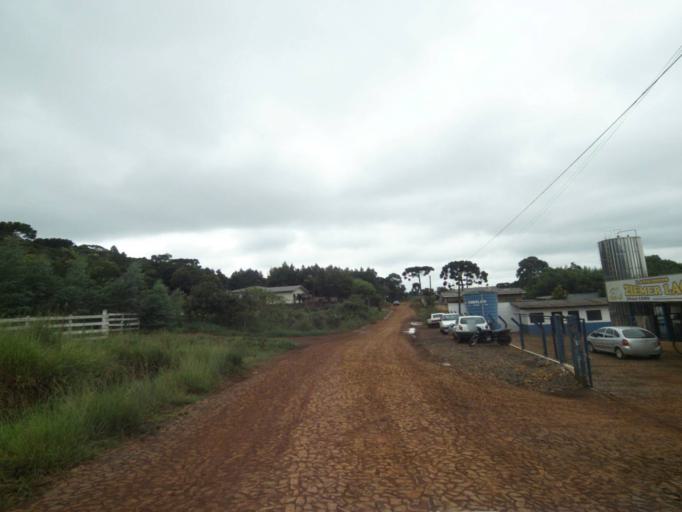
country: BR
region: Parana
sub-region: Pitanga
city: Pitanga
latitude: -24.9342
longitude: -51.8676
